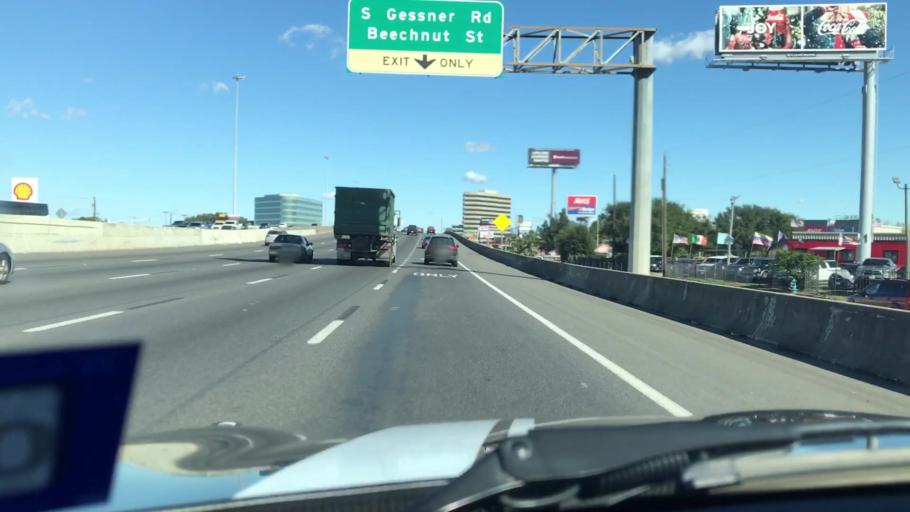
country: US
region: Texas
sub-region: Fort Bend County
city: Meadows Place
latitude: 29.6737
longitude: -95.5441
